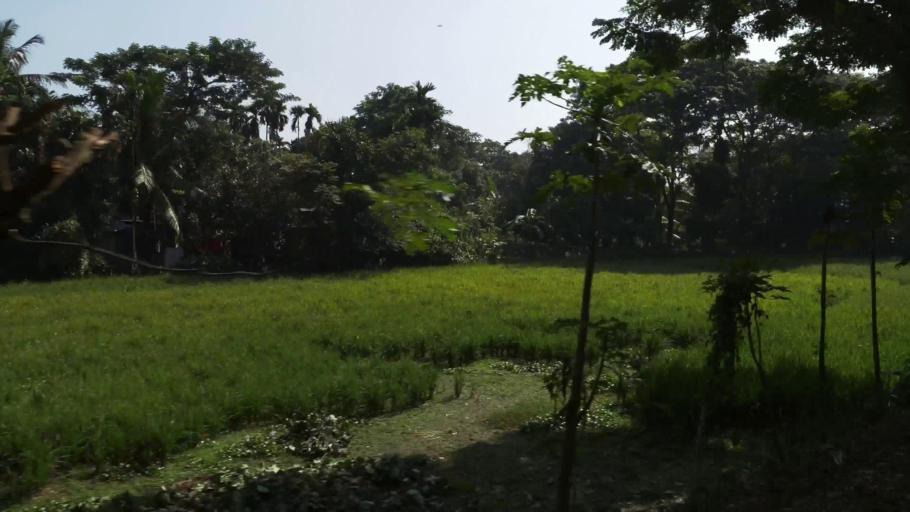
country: BD
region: Dhaka
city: Gafargaon
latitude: 24.5972
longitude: 90.4975
